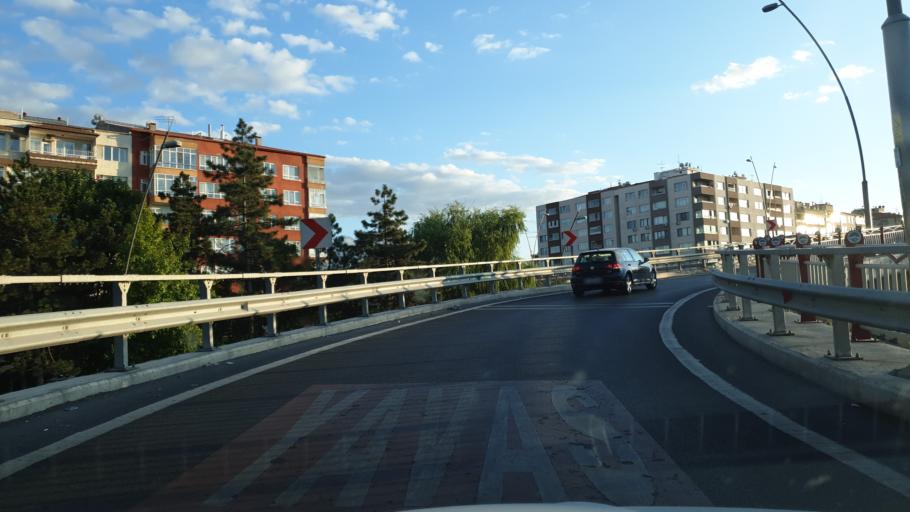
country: TR
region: Kayseri
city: Kayseri
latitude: 38.7337
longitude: 35.4950
